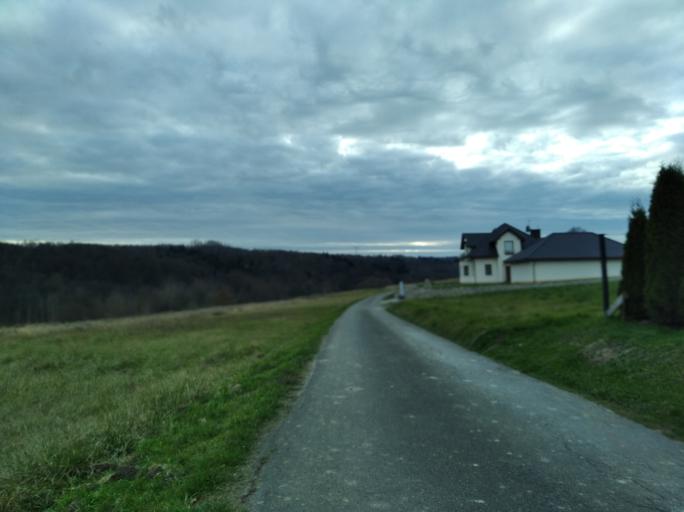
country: PL
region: Subcarpathian Voivodeship
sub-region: Powiat brzozowski
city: Domaradz
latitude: 49.7851
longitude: 21.9413
